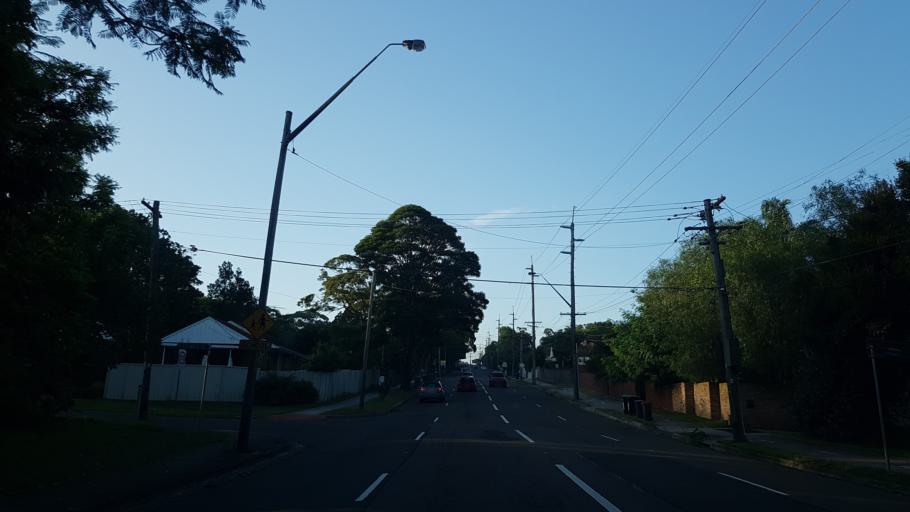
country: AU
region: New South Wales
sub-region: Warringah
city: Narraweena
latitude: -33.7490
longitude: 151.2619
